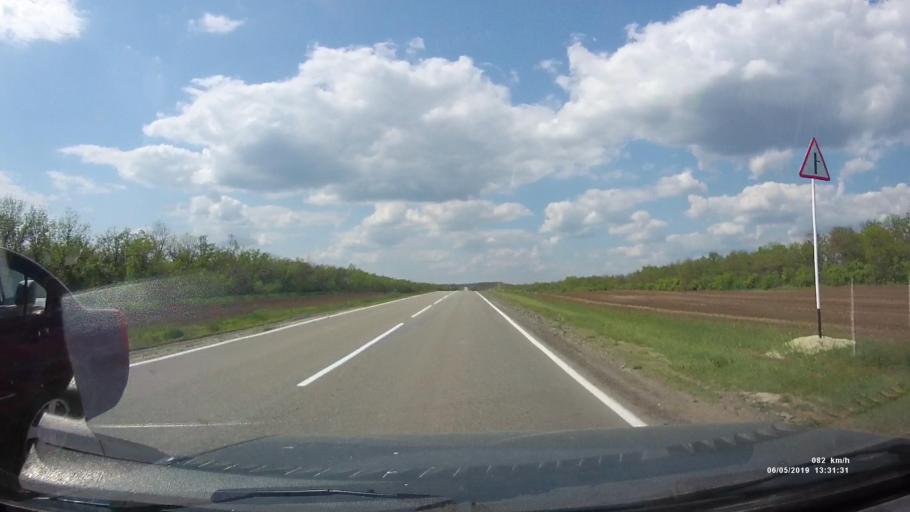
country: RU
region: Rostov
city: Ust'-Donetskiy
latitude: 47.6772
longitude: 40.8097
